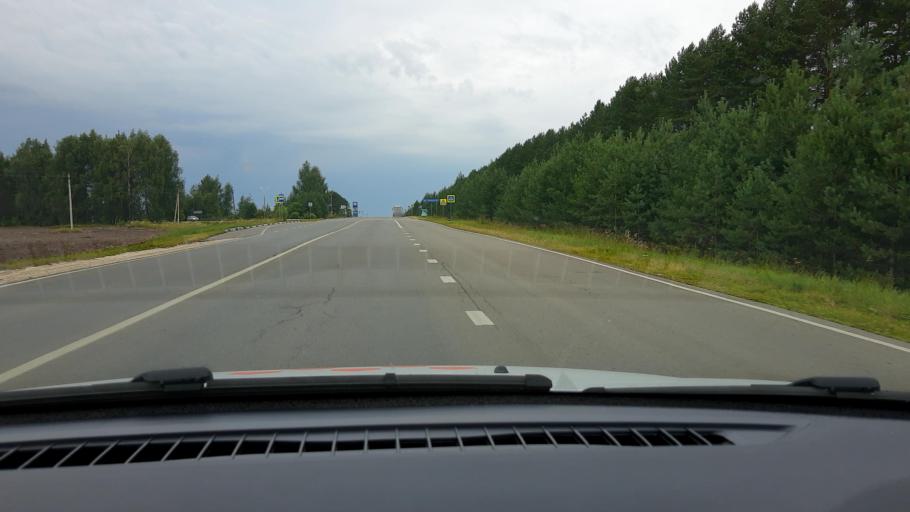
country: RU
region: Nizjnij Novgorod
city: Vyyezdnoye
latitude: 55.1521
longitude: 43.5711
